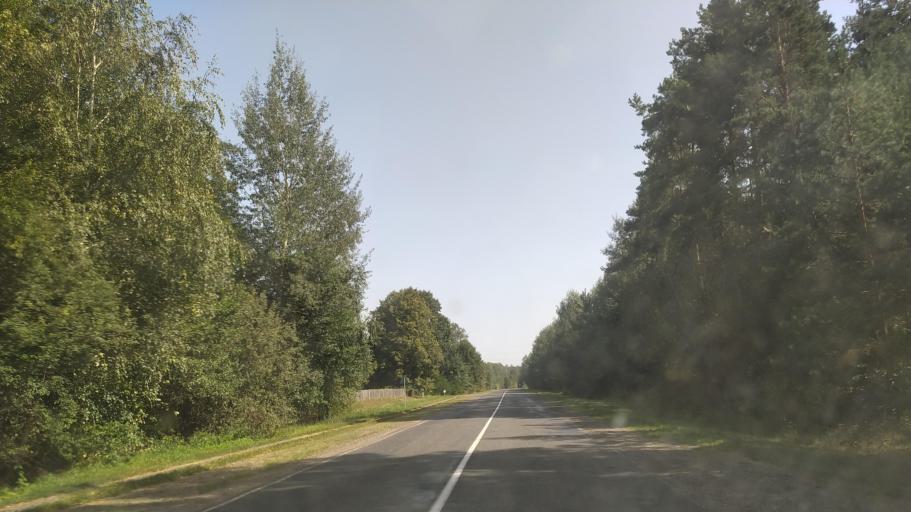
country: BY
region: Brest
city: Byaroza
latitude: 52.4159
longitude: 24.9830
